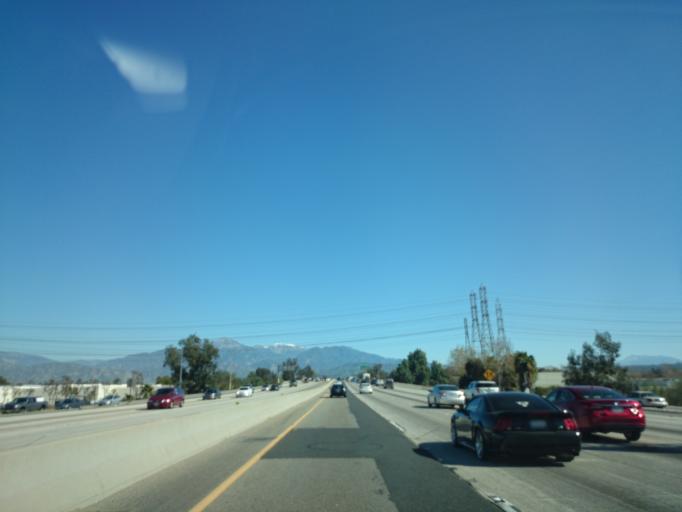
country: US
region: California
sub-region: San Bernardino County
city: Loma Linda
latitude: 34.0666
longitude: -117.2414
